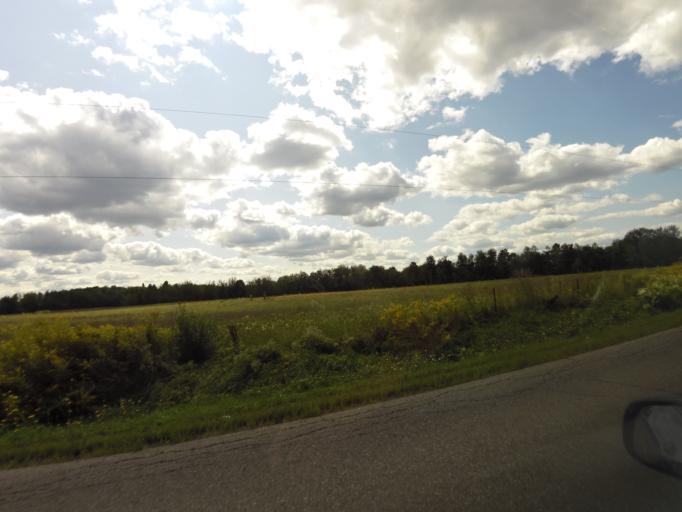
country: CA
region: Ontario
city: Ottawa
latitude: 45.3941
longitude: -75.5612
